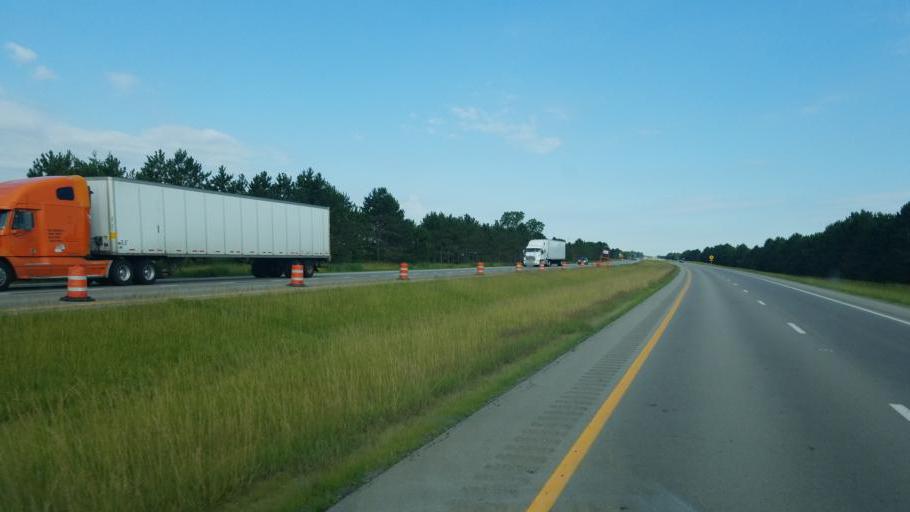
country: US
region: Ohio
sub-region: Wyandot County
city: Carey
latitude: 40.9502
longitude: -83.4229
